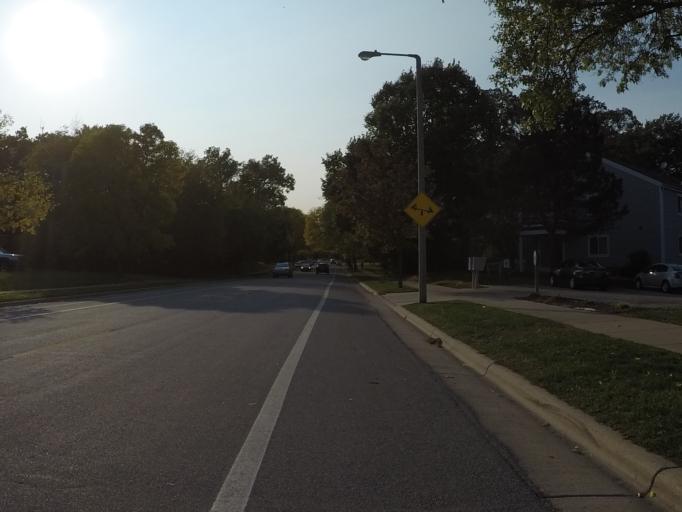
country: US
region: Wisconsin
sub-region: Dane County
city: Middleton
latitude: 43.0642
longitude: -89.5143
